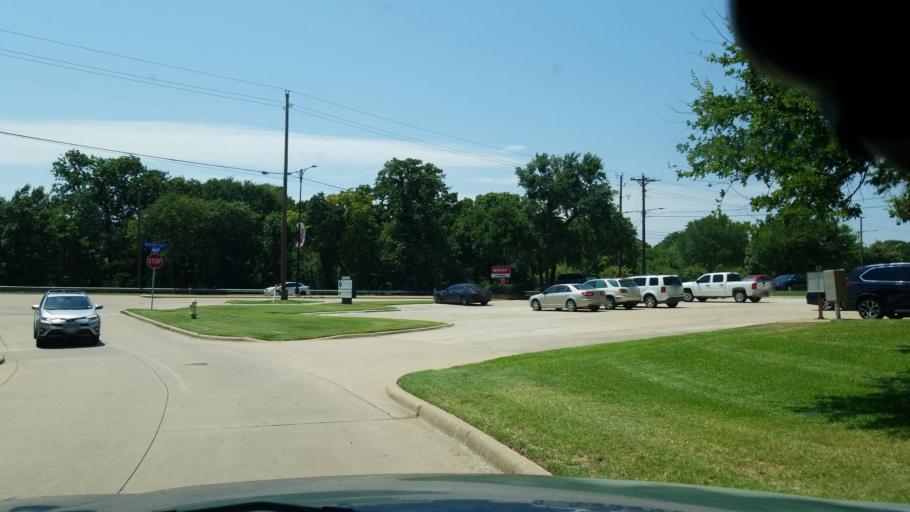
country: US
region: Texas
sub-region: Dallas County
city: Coppell
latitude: 32.9563
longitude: -96.9928
